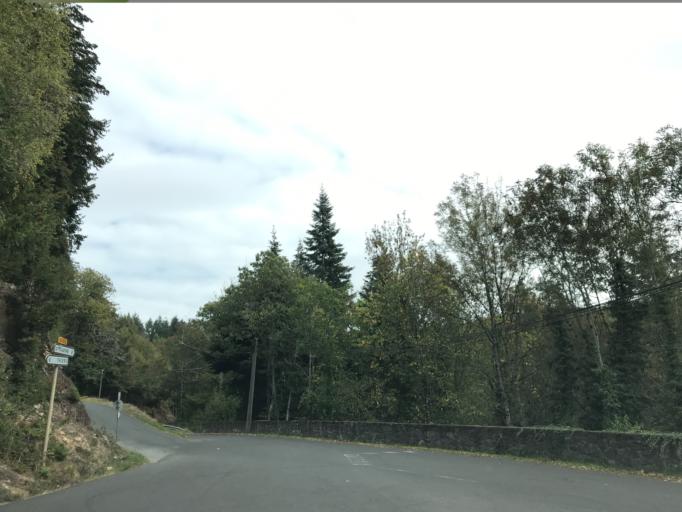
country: FR
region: Auvergne
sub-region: Departement du Puy-de-Dome
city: Thiers
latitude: 45.8353
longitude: 3.5770
